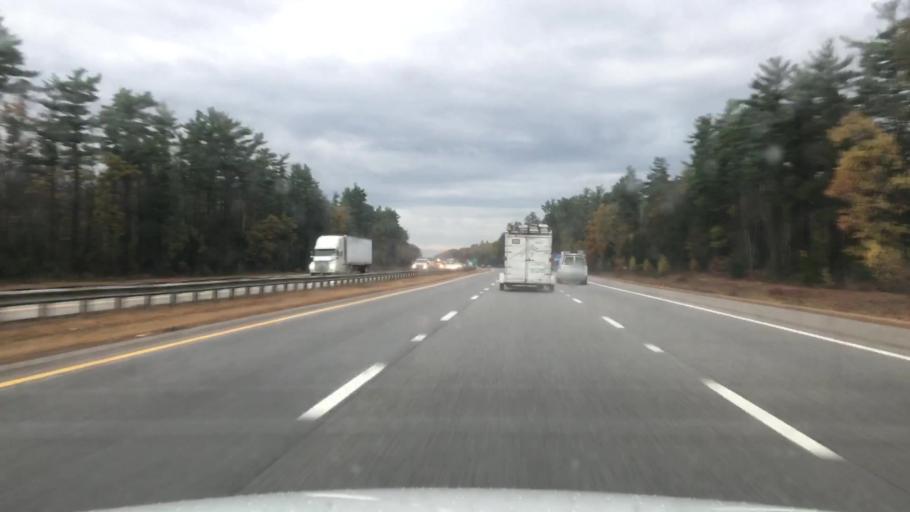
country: US
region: Maine
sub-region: York County
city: West Kennebunk
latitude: 43.4260
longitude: -70.5506
